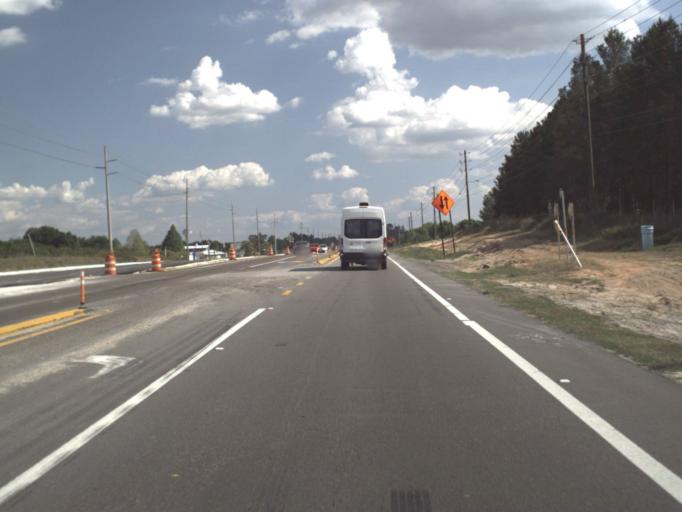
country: US
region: Florida
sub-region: Lake County
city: Four Corners
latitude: 28.4230
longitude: -81.7084
